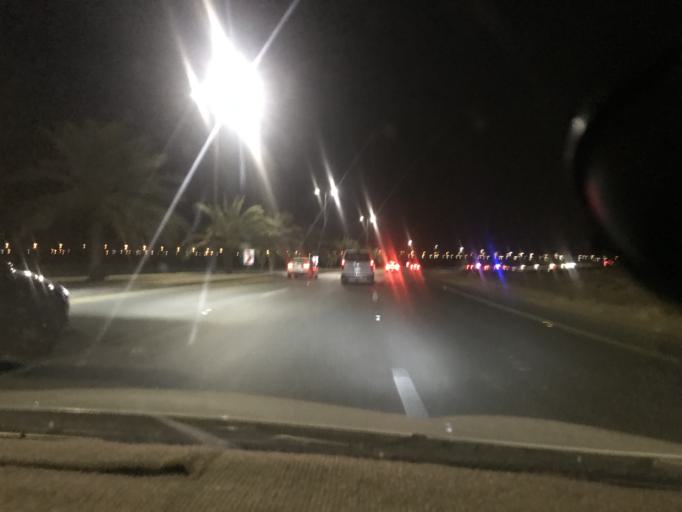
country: SA
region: Al-Qassim
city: Buraydah
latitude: 26.4065
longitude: 43.9600
